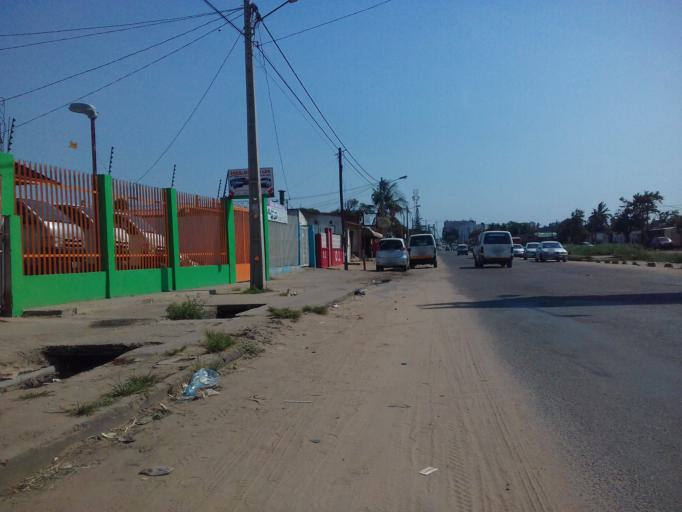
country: MZ
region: Maputo City
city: Maputo
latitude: -25.9475
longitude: 32.5711
